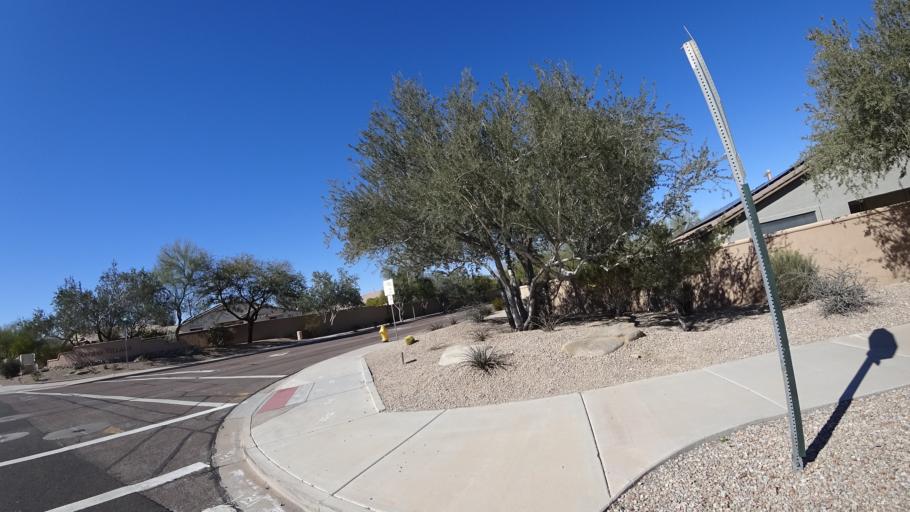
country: US
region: Arizona
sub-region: Maricopa County
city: Goodyear
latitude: 33.3539
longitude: -112.4448
